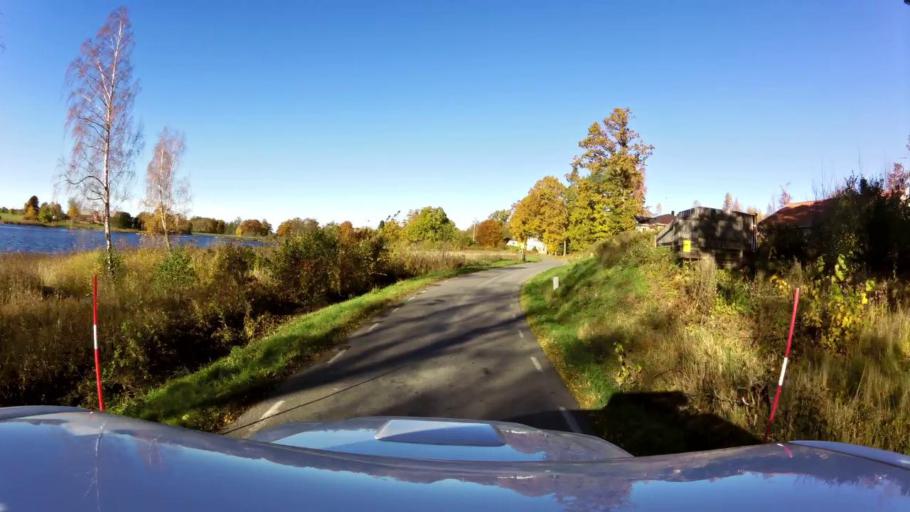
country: SE
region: OEstergoetland
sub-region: Linkopings Kommun
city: Ljungsbro
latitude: 58.5289
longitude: 15.4584
